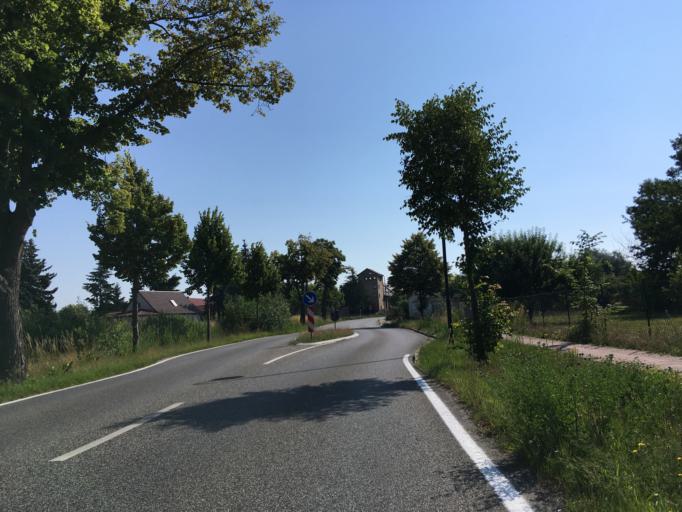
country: DE
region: Brandenburg
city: Wandlitz
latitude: 52.7831
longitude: 13.3804
